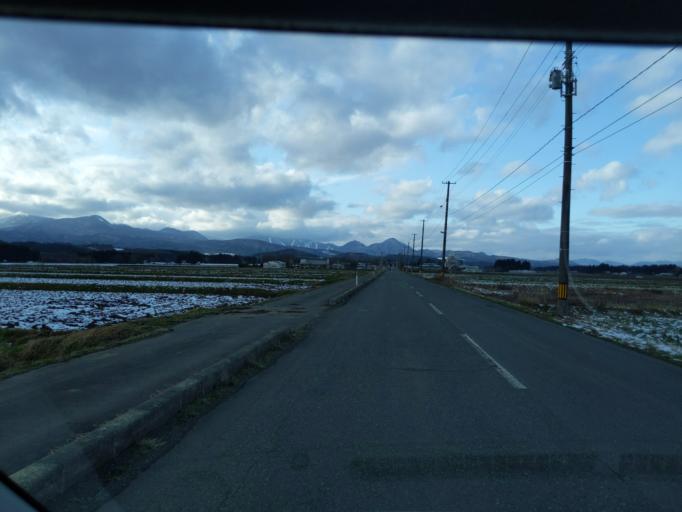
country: JP
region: Iwate
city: Kitakami
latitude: 39.2016
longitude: 141.0572
